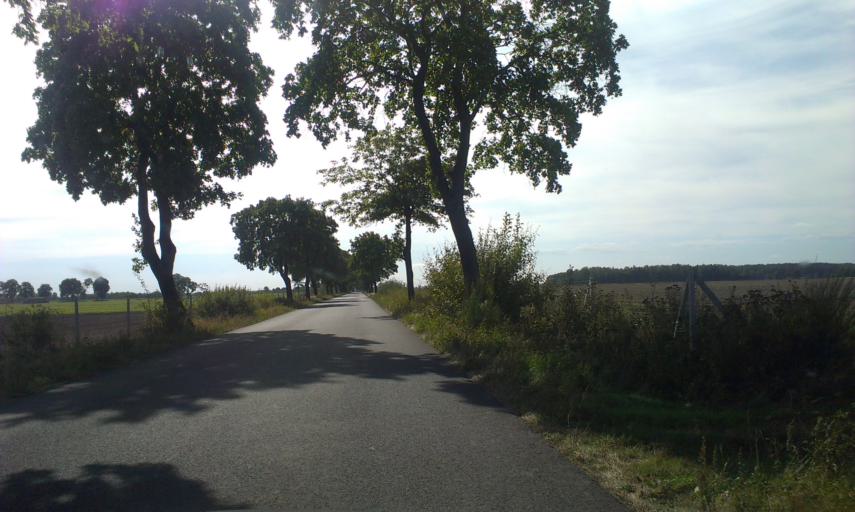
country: PL
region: Greater Poland Voivodeship
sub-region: Powiat zlotowski
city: Zlotow
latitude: 53.4728
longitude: 16.9903
